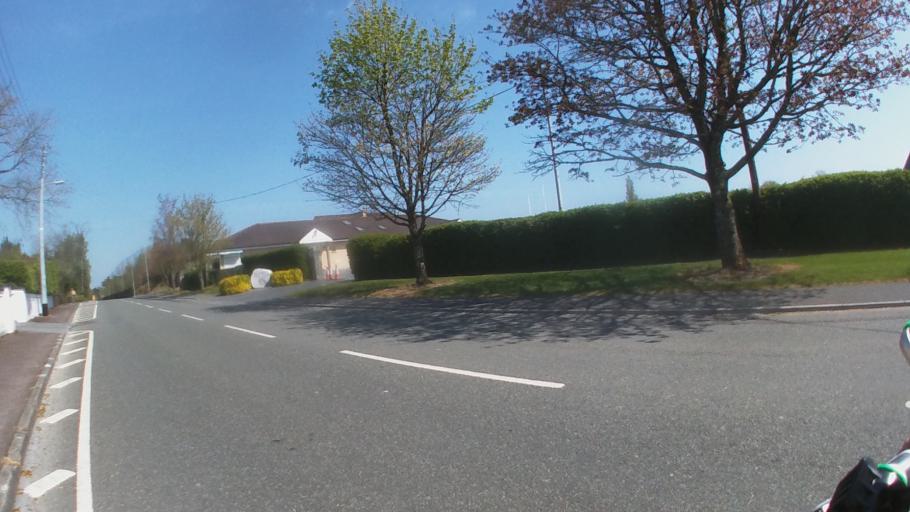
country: IE
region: Leinster
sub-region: Kilkenny
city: Kilkenny
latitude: 52.6708
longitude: -7.2503
